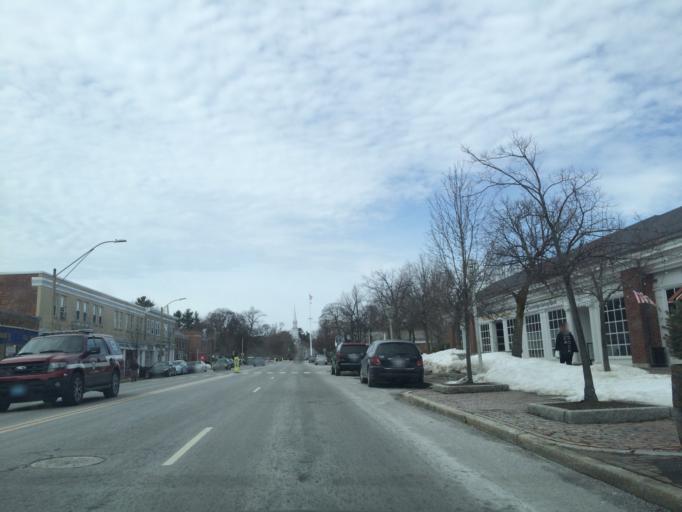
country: US
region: Massachusetts
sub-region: Middlesex County
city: Lexington
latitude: 42.4476
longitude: -71.2276
